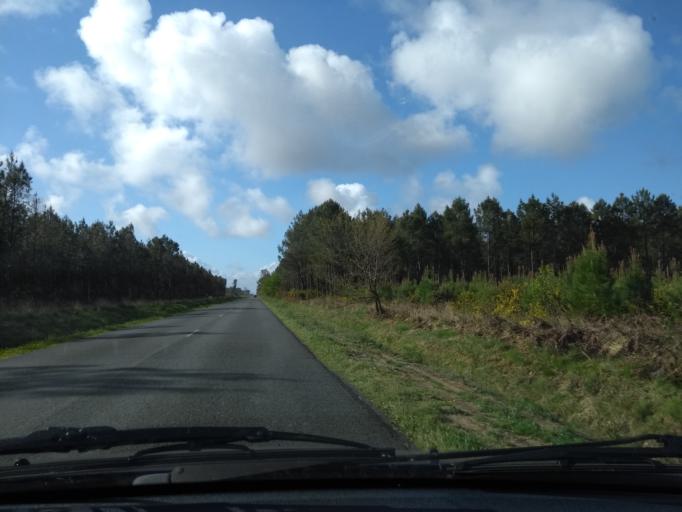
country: FR
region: Aquitaine
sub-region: Departement des Landes
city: Sanguinet
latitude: 44.4541
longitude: -1.0706
